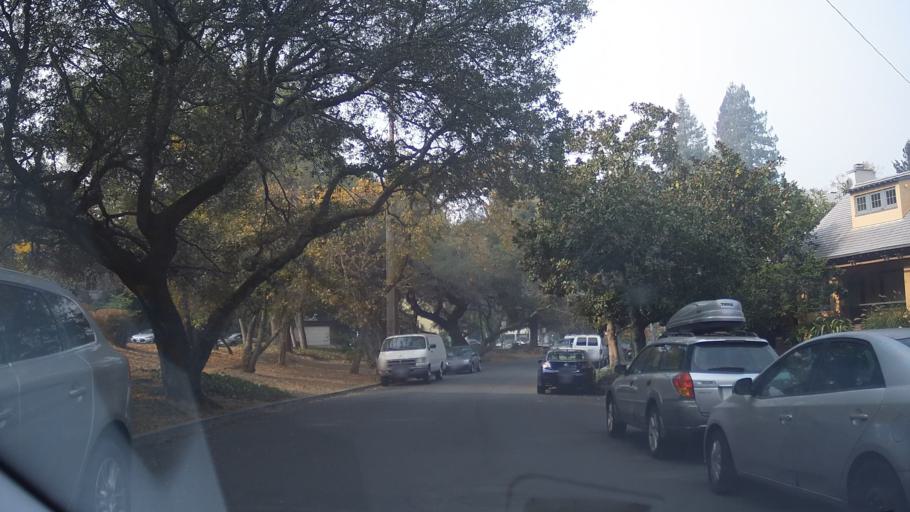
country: US
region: California
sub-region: Alameda County
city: Berkeley
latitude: 37.8540
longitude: -122.2456
